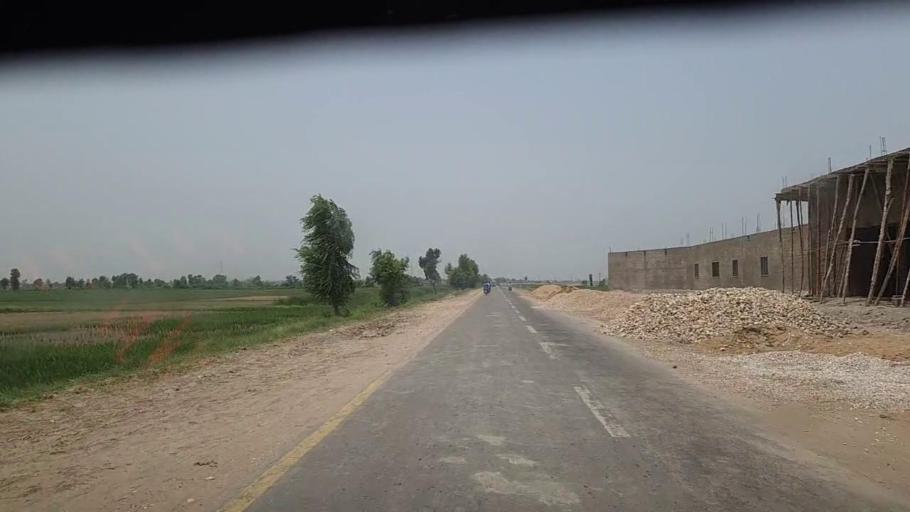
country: PK
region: Sindh
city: Sita Road
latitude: 27.0408
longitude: 67.8671
